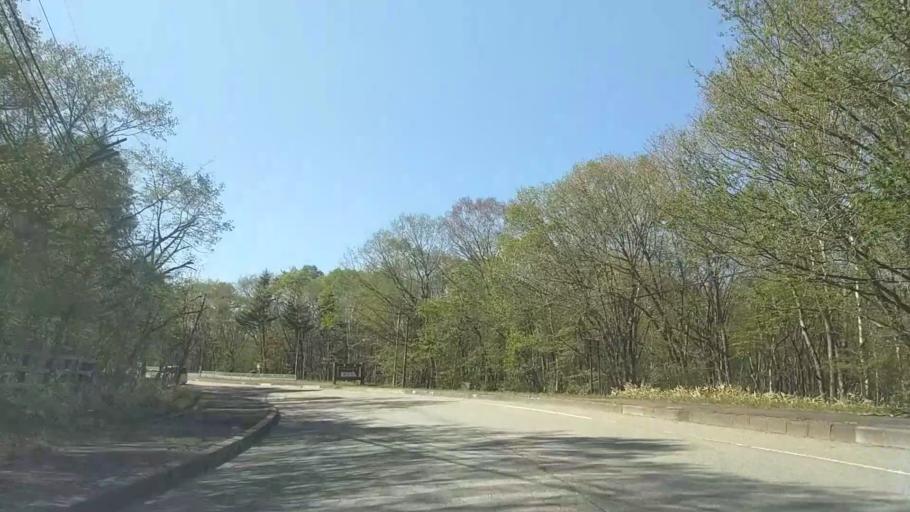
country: JP
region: Yamanashi
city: Nirasaki
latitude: 35.9388
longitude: 138.4415
